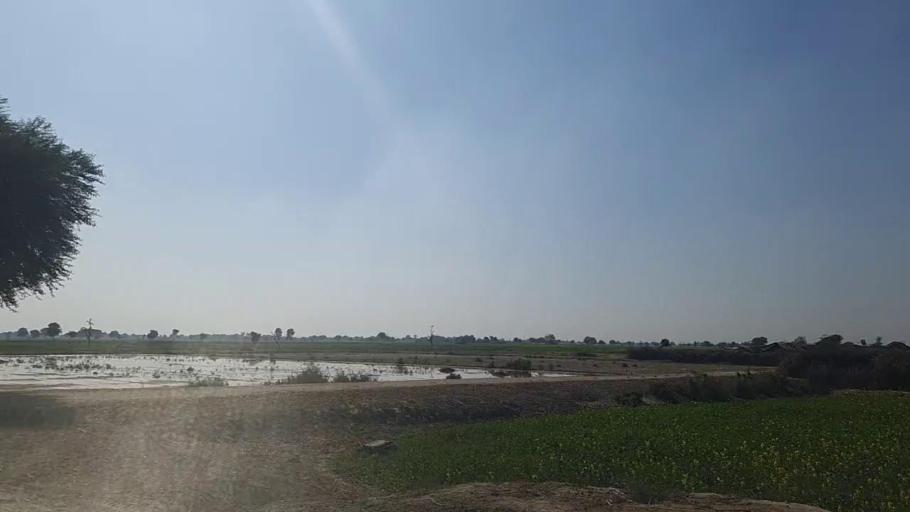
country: PK
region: Sindh
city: Jam Sahib
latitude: 26.2177
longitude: 68.5840
